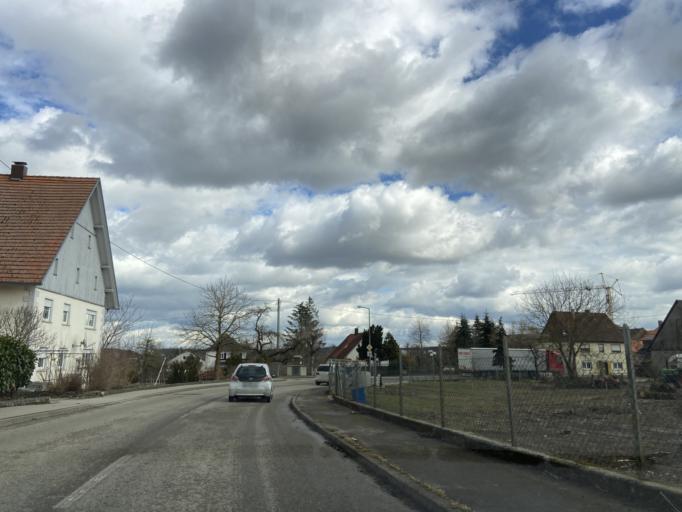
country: DE
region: Baden-Wuerttemberg
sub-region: Tuebingen Region
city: Ostrach
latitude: 47.9631
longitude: 9.3183
